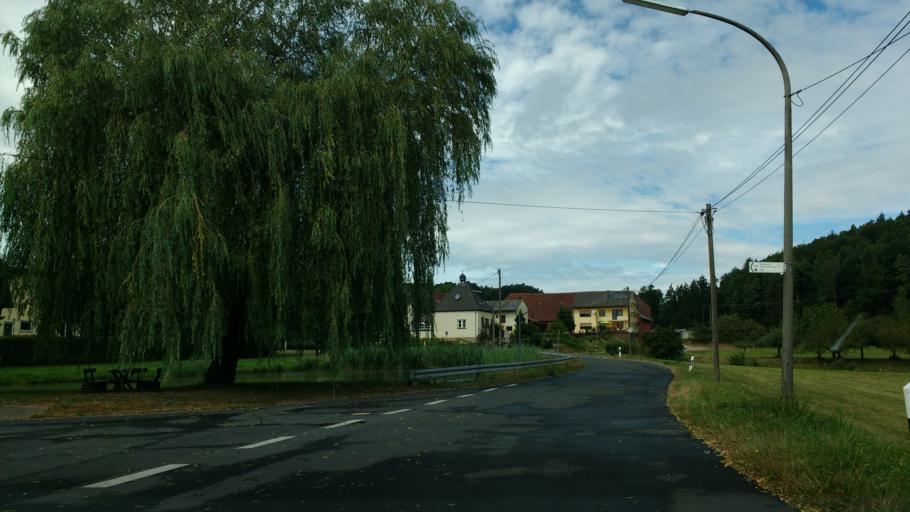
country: DE
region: Bavaria
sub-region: Regierungsbezirk Unterfranken
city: Geiselwind
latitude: 49.7815
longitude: 10.5245
